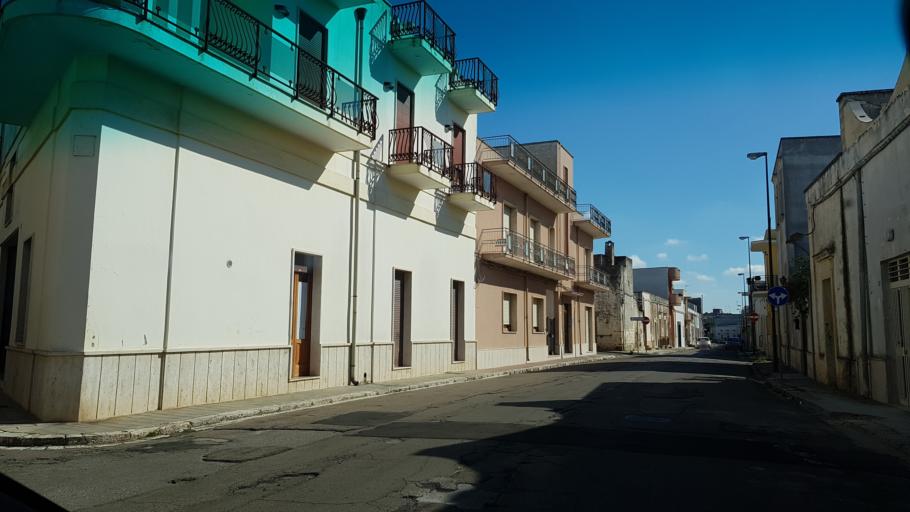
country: IT
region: Apulia
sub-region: Provincia di Lecce
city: Campi Salentina
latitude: 40.3995
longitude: 18.0132
